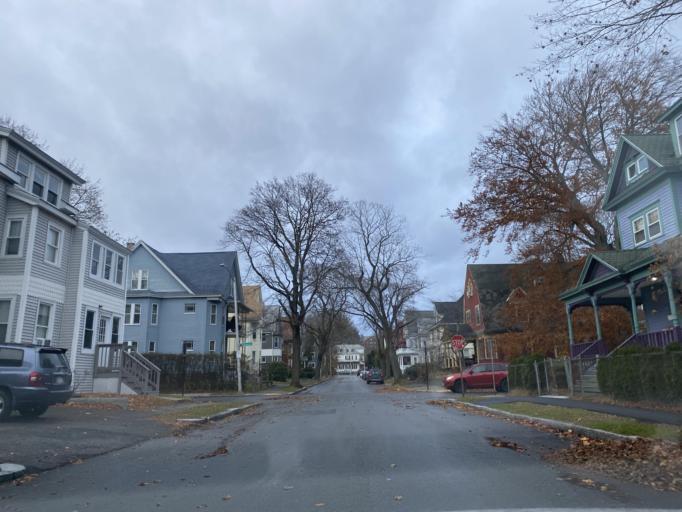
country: US
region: Massachusetts
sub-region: Worcester County
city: Worcester
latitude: 42.2692
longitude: -71.8101
